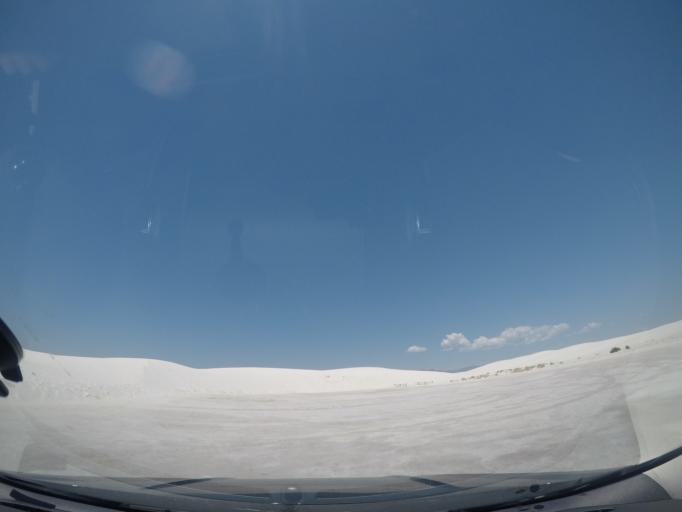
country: US
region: New Mexico
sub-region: Otero County
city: Holloman Air Force Base
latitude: 32.8181
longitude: -106.2708
